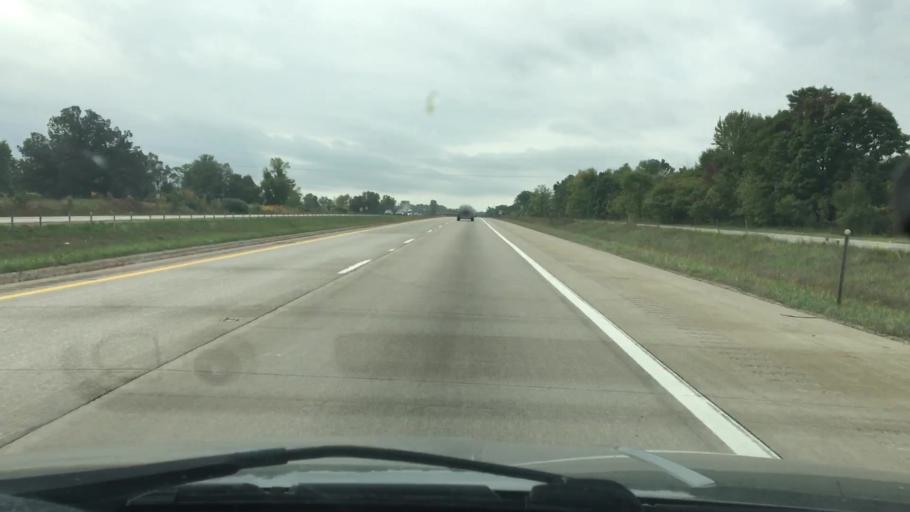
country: US
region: Michigan
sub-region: Genesee County
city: Fenton
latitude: 42.6870
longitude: -83.7607
